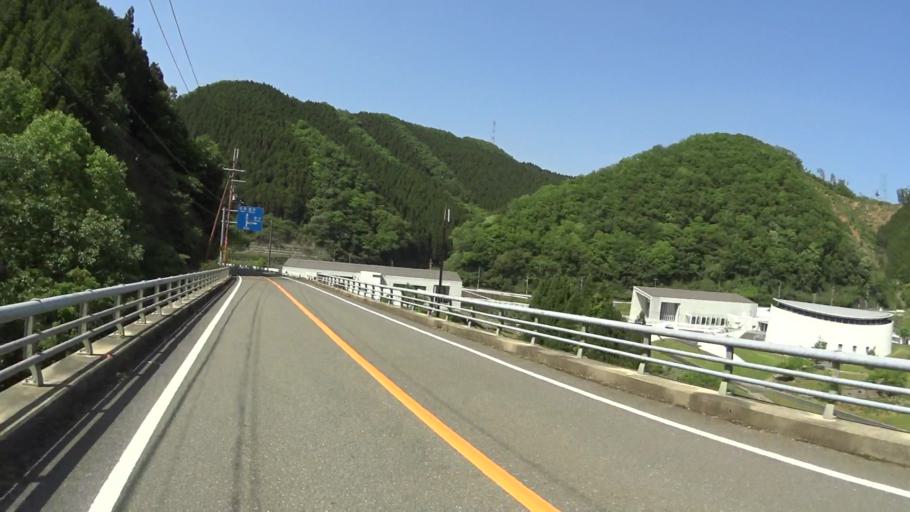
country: JP
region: Kyoto
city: Kameoka
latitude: 35.1496
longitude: 135.5123
